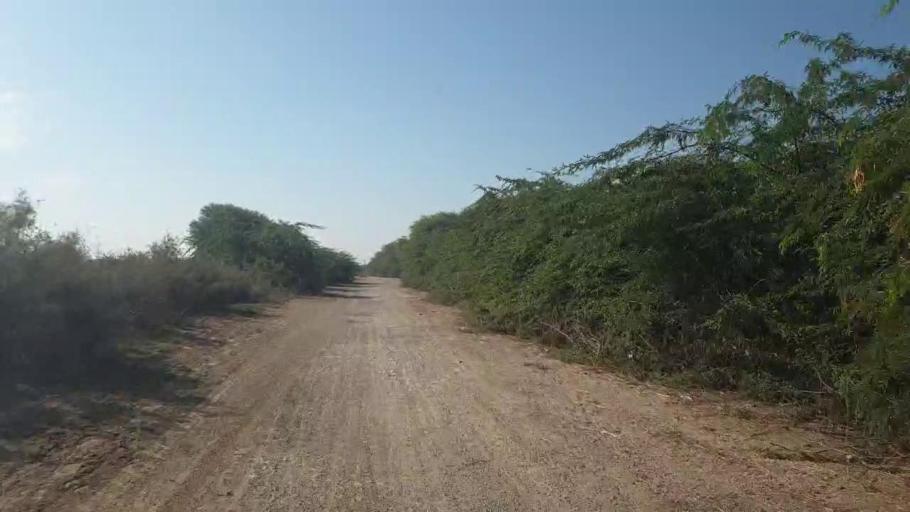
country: PK
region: Sindh
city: Rajo Khanani
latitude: 24.9555
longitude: 68.7955
